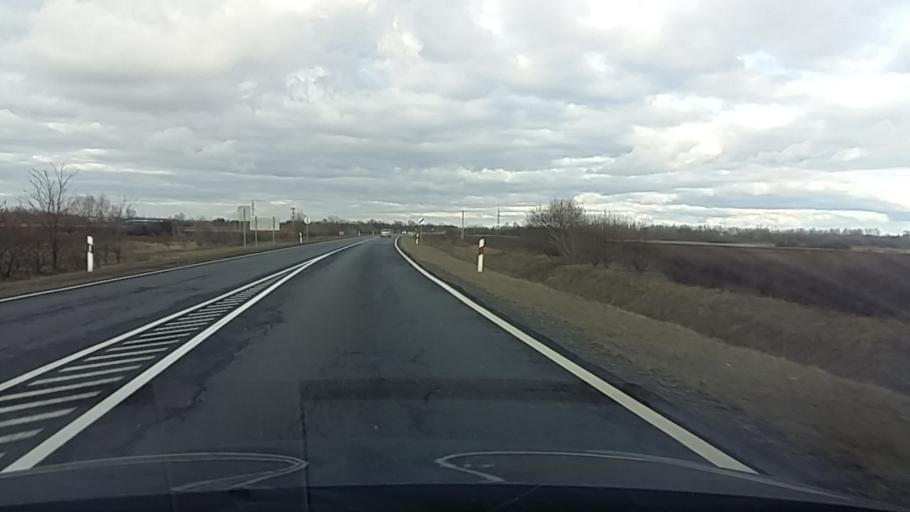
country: HU
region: Szabolcs-Szatmar-Bereg
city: Napkor
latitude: 47.9366
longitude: 21.8185
